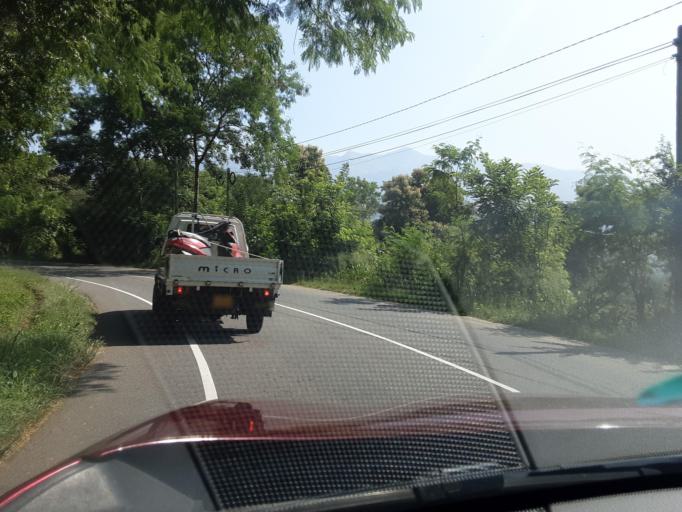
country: LK
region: Uva
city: Badulla
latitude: 7.1496
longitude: 81.0579
